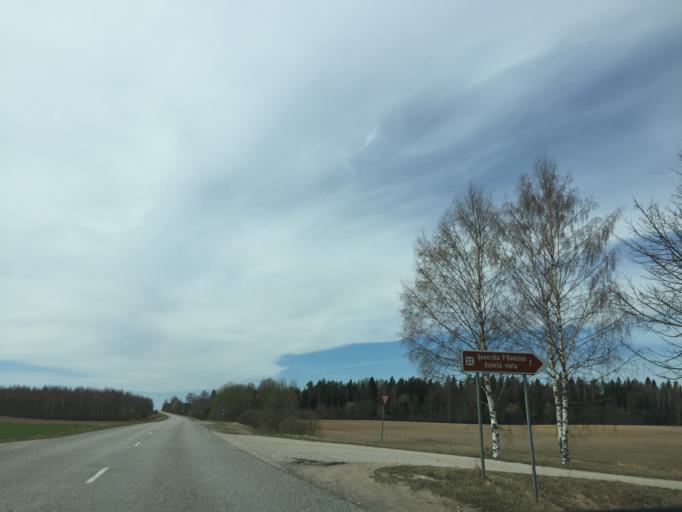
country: LV
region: Valkas Rajons
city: Valka
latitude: 57.7805
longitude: 25.9500
